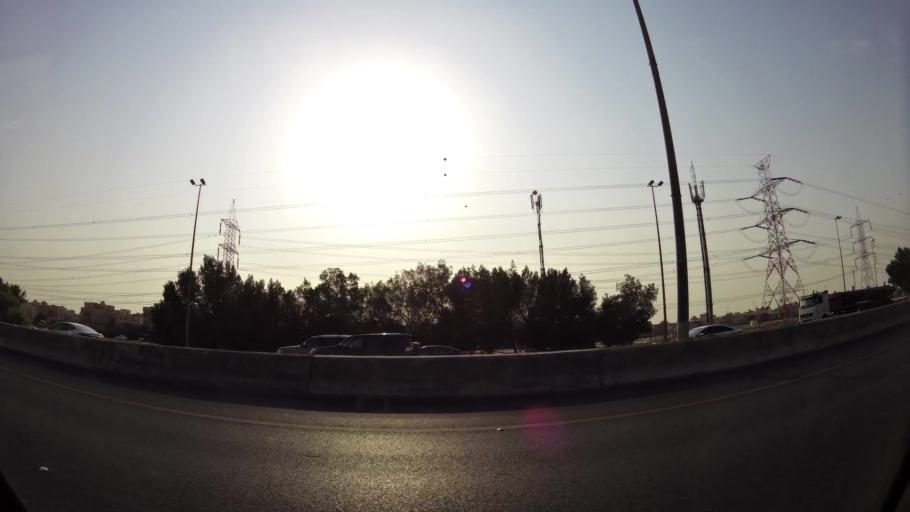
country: KW
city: Bayan
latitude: 29.2892
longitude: 48.0303
